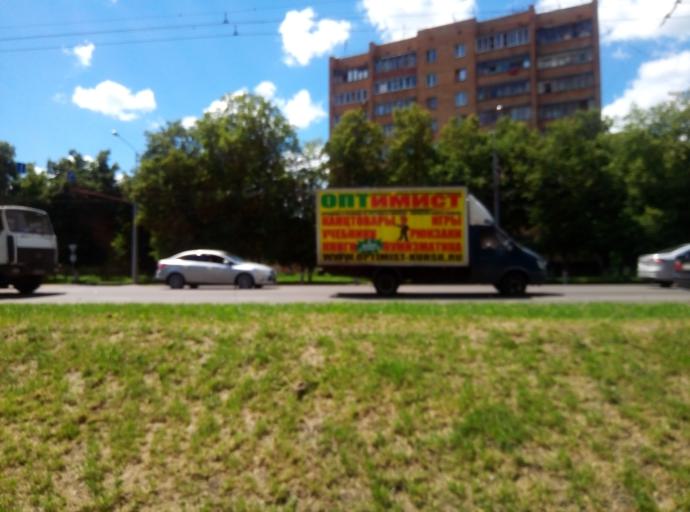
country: RU
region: Kursk
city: Kursk
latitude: 51.7673
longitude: 36.1832
